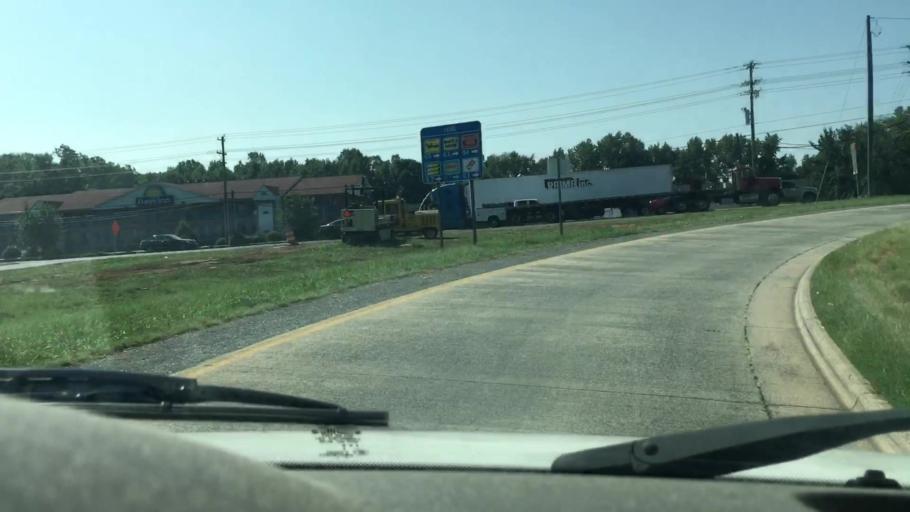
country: US
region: North Carolina
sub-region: Mecklenburg County
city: Charlotte
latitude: 35.3083
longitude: -80.8465
